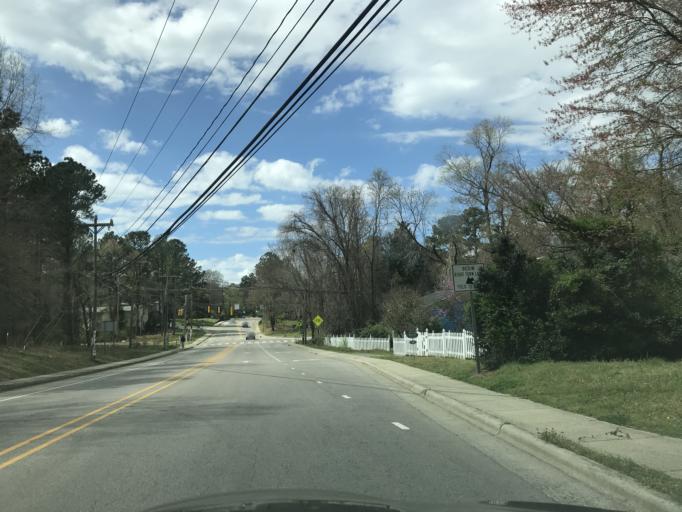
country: US
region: North Carolina
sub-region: Orange County
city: Carrboro
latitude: 35.9170
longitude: -79.0740
